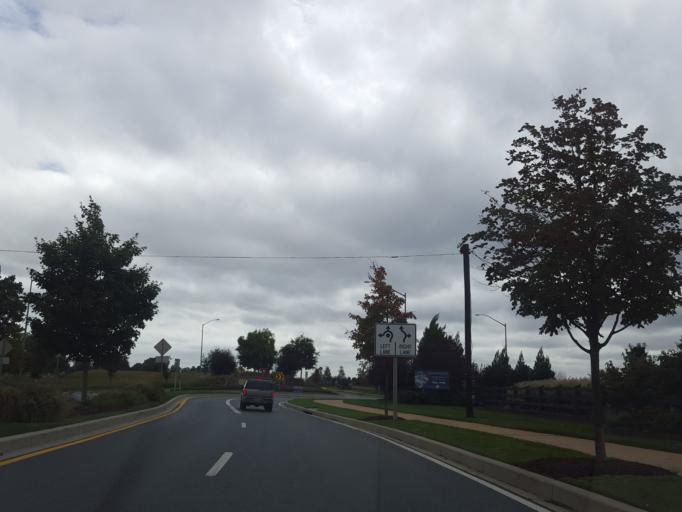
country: US
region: Maryland
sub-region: Frederick County
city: Brunswick
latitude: 39.3353
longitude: -77.6377
